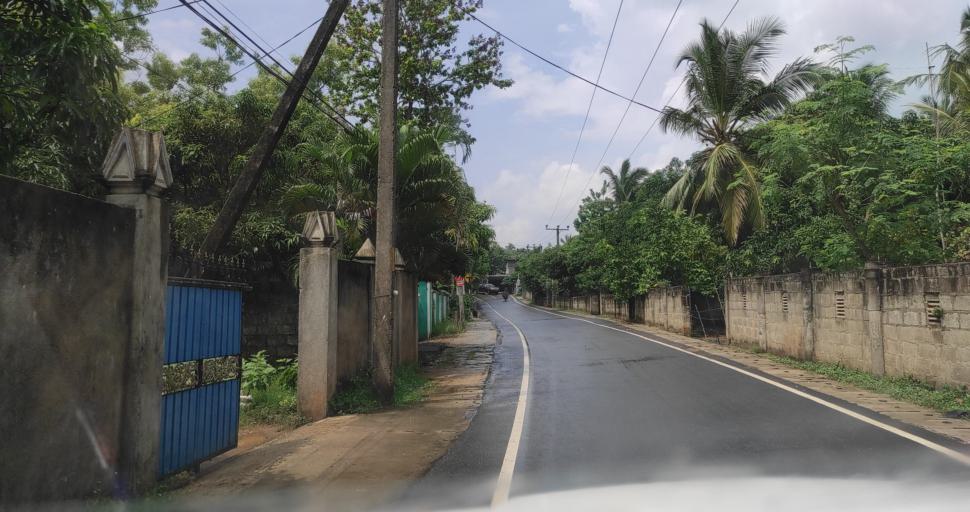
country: LK
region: Eastern Province
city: Trincomalee
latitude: 8.3748
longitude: 81.0081
